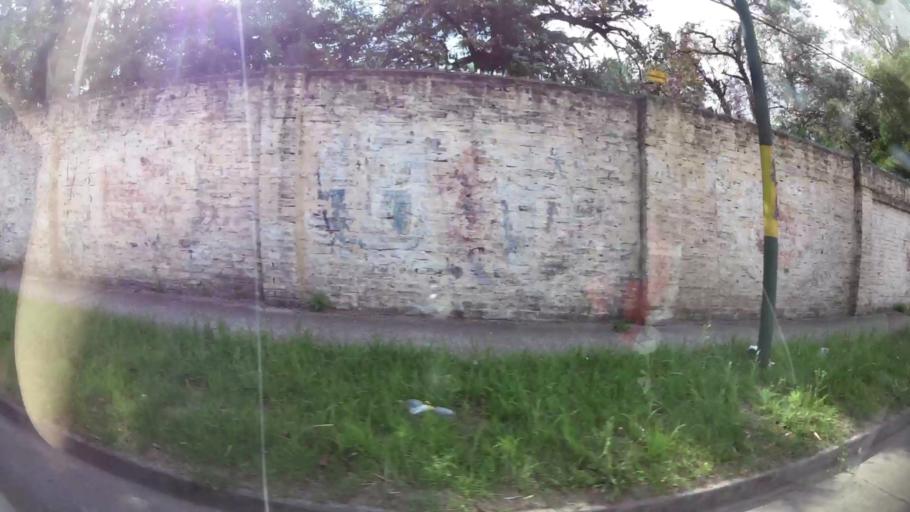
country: AR
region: Buenos Aires
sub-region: Partido de Merlo
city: Merlo
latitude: -34.6362
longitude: -58.7137
